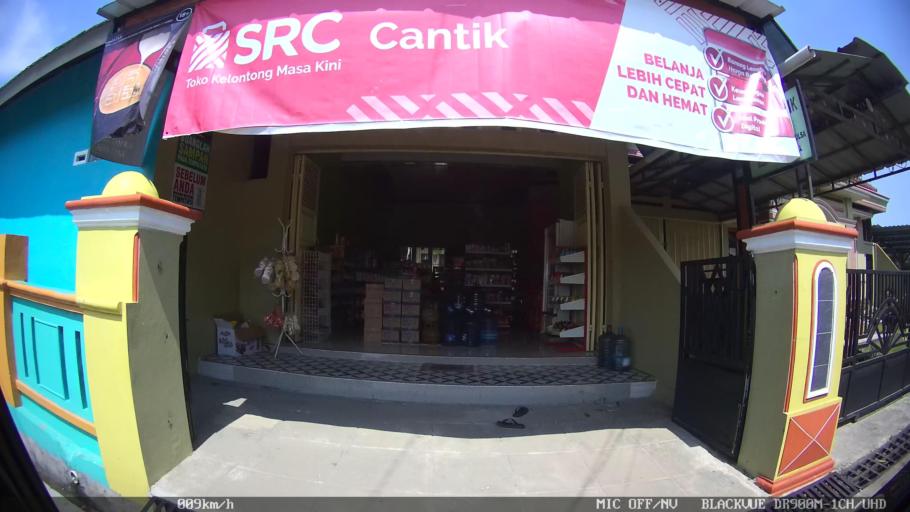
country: ID
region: Lampung
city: Kedaton
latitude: -5.3700
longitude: 105.2523
